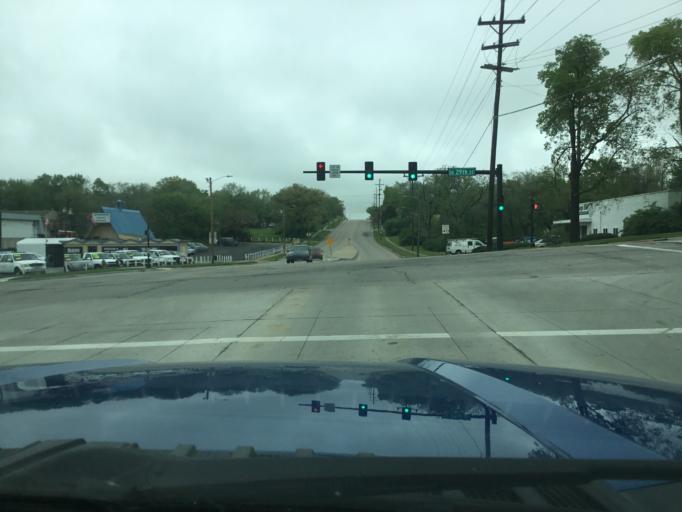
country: US
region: Kansas
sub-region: Shawnee County
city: Topeka
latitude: 39.0150
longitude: -95.6702
